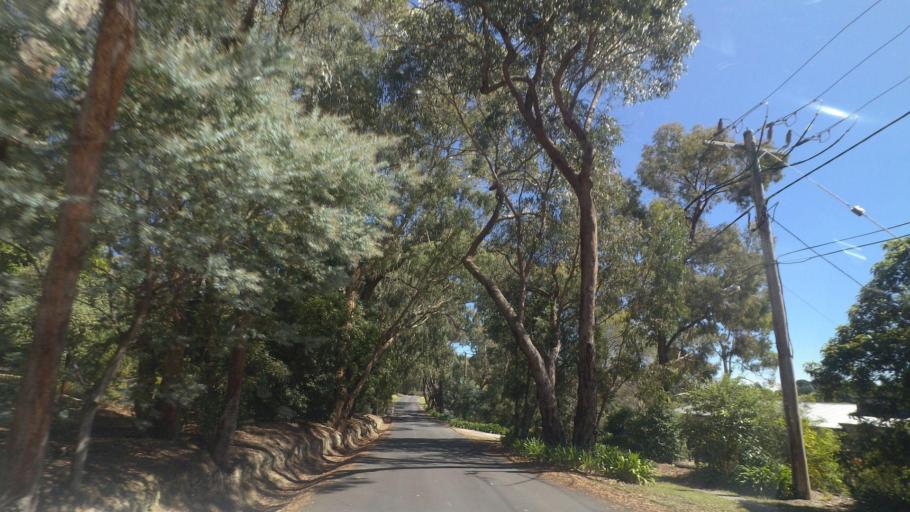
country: AU
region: Victoria
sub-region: Manningham
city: Donvale
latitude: -37.7891
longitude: 145.1906
